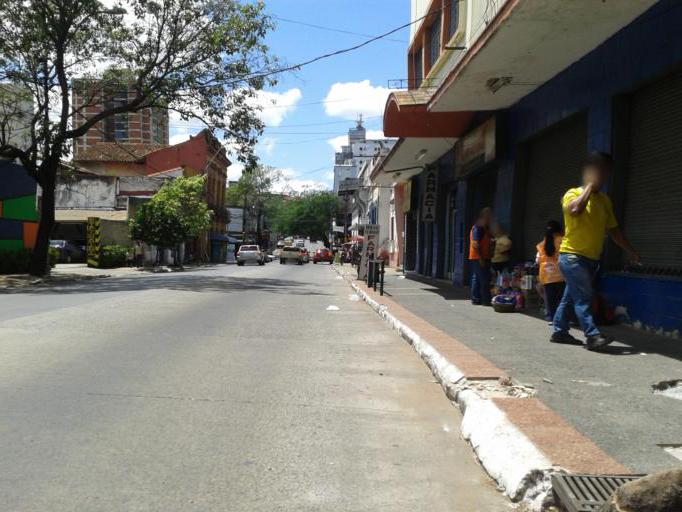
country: PY
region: Asuncion
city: Asuncion
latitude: -25.2893
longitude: -57.6287
